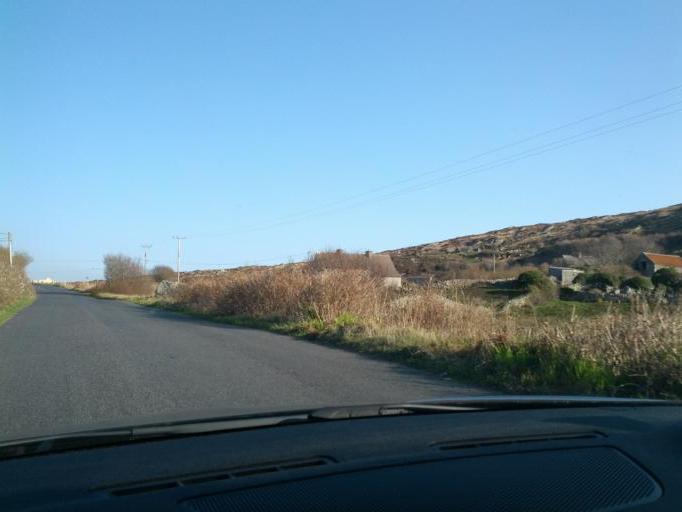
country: IE
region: Connaught
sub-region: County Galway
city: Clifden
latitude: 53.3350
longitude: -9.8516
